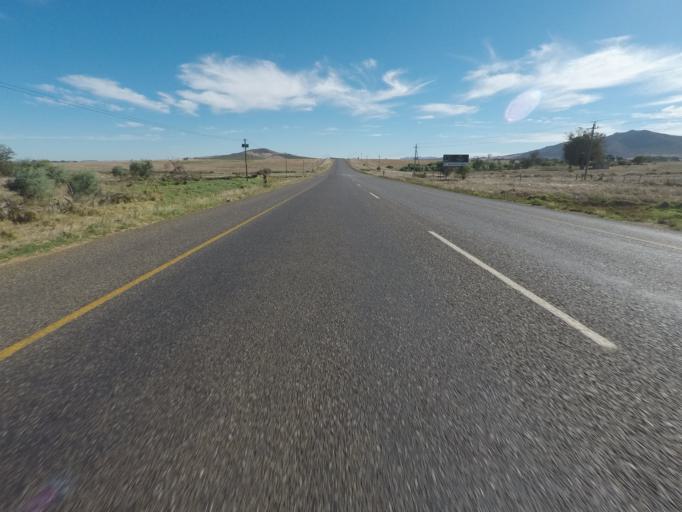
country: ZA
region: Western Cape
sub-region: West Coast District Municipality
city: Malmesbury
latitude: -33.6150
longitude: 18.7270
